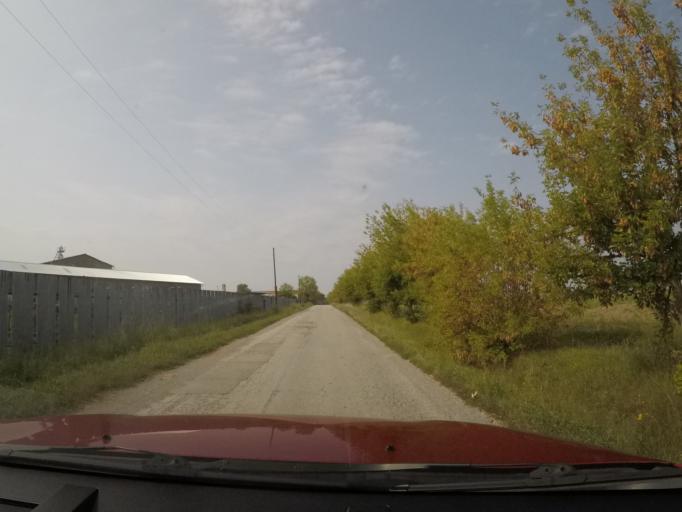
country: SK
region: Kosicky
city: Moldava nad Bodvou
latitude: 48.5892
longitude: 21.0165
